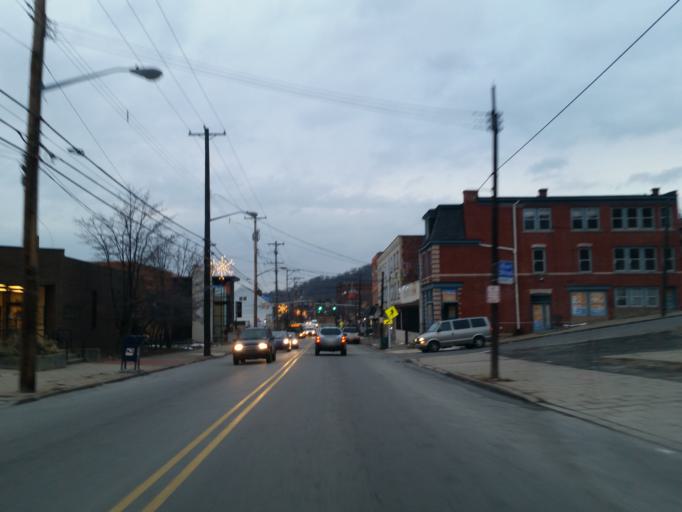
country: US
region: Pennsylvania
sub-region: Allegheny County
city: Homestead
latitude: 40.4075
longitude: -79.9434
